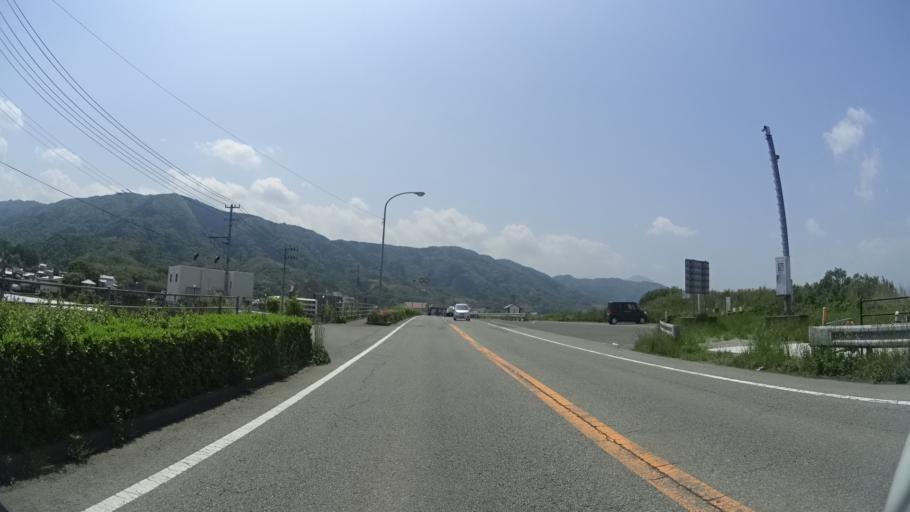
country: JP
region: Tokushima
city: Kamojimacho-jogejima
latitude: 34.0640
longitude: 134.3179
